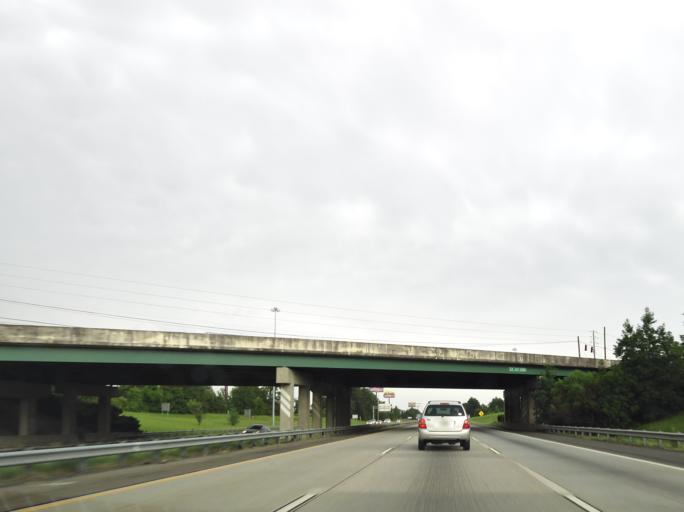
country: US
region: Georgia
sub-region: Peach County
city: Byron
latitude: 32.6131
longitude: -83.7430
